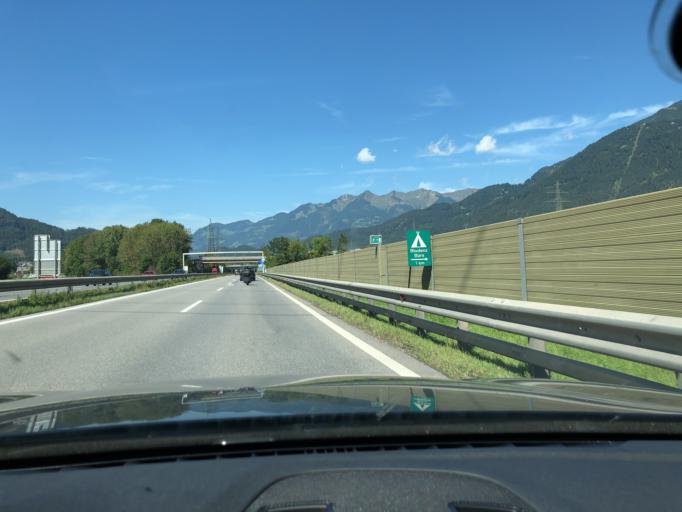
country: AT
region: Vorarlberg
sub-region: Politischer Bezirk Bludenz
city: Bludenz
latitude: 47.1433
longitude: 9.8225
